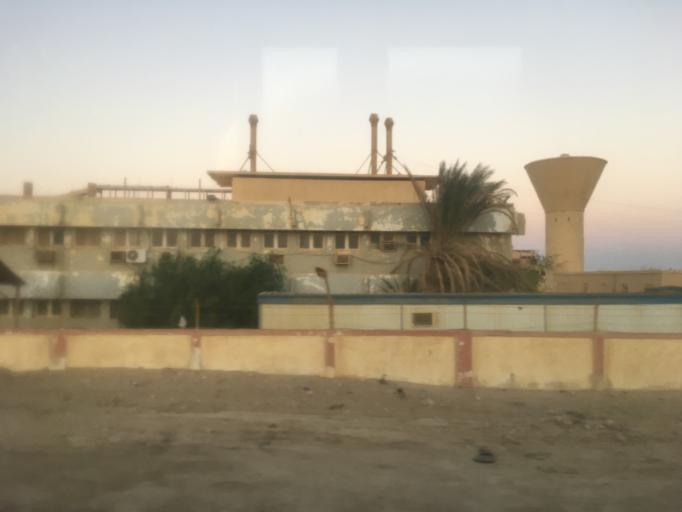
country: EG
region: Red Sea
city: Al Qusayr
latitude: 26.2566
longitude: 34.1994
